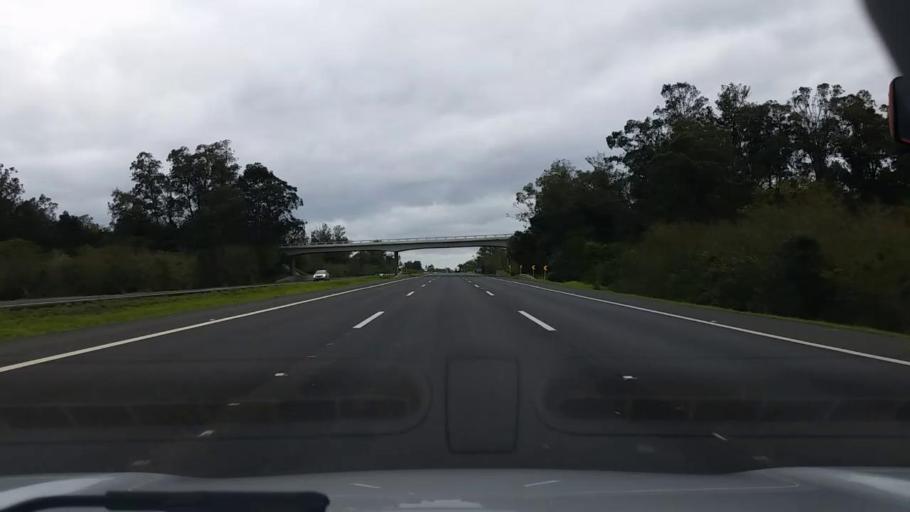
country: BR
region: Rio Grande do Sul
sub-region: Rolante
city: Rolante
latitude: -29.8834
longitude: -50.5463
